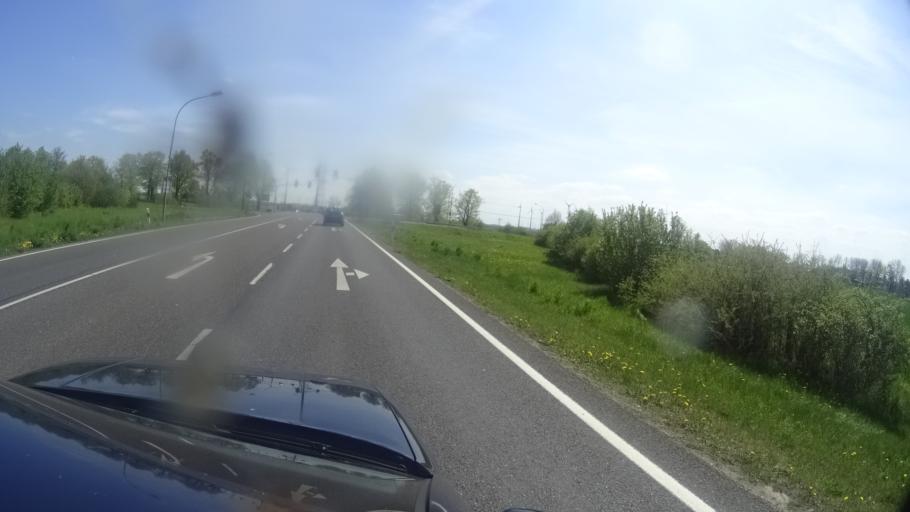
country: DE
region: Brandenburg
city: Nauen
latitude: 52.6011
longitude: 12.8506
